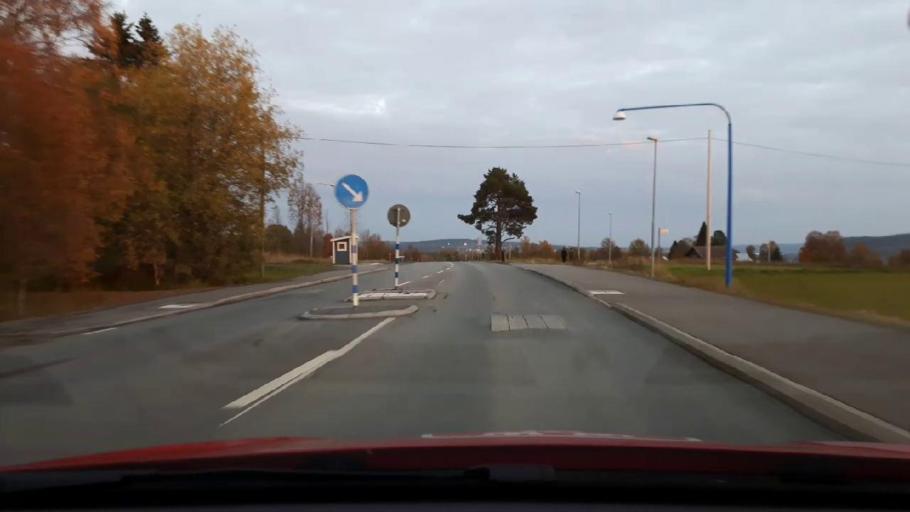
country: SE
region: Jaemtland
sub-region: OEstersunds Kommun
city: Ostersund
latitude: 63.2309
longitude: 14.5834
